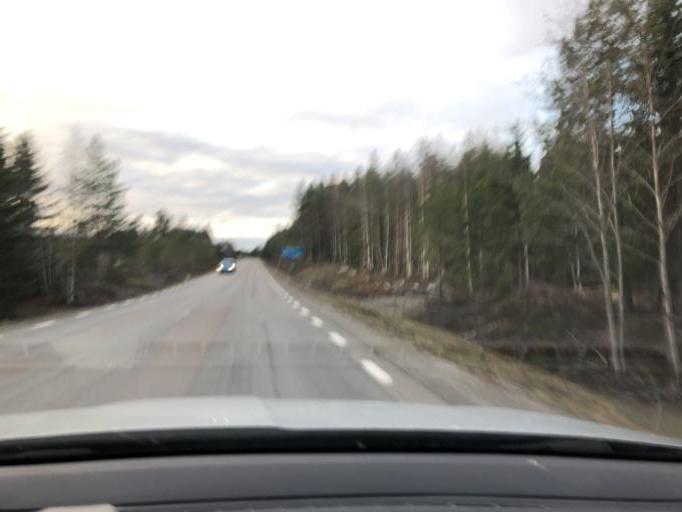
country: SE
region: Gaevleborg
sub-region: Hudiksvalls Kommun
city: Iggesund
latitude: 61.5519
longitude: 16.9857
